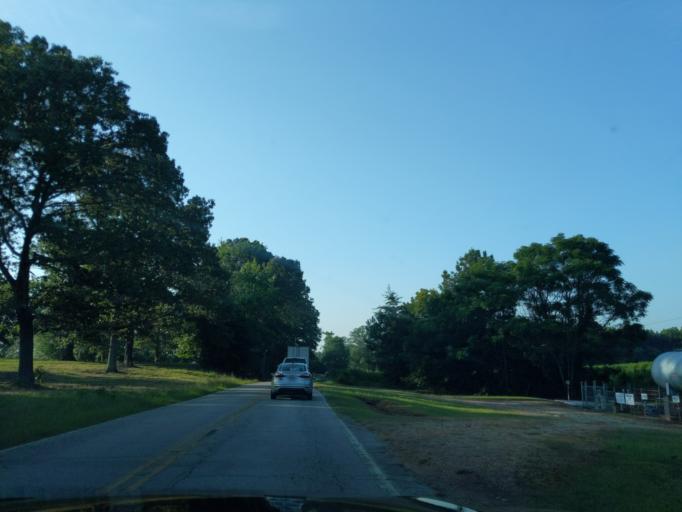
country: US
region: South Carolina
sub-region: Spartanburg County
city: Roebuck
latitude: 34.8243
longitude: -81.9872
